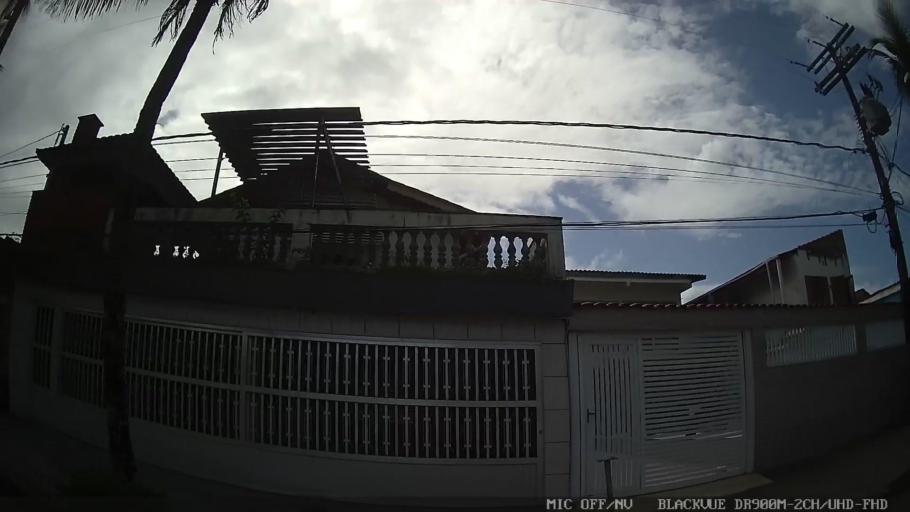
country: BR
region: Sao Paulo
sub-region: Itanhaem
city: Itanhaem
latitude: -24.1427
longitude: -46.7117
